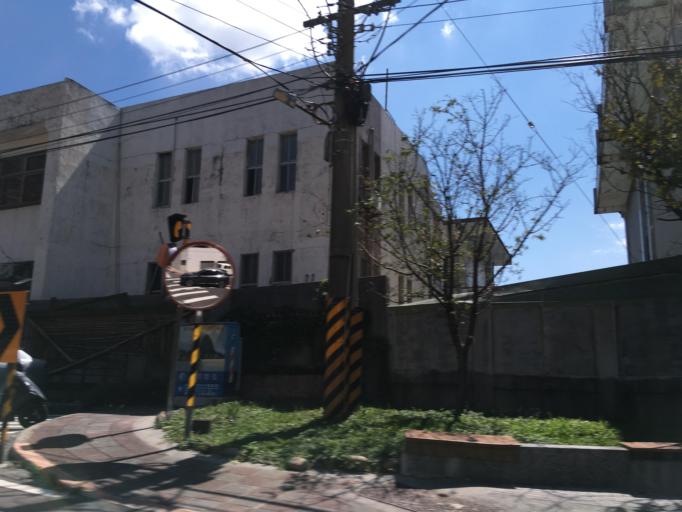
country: TW
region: Taipei
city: Taipei
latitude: 25.1444
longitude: 121.5028
